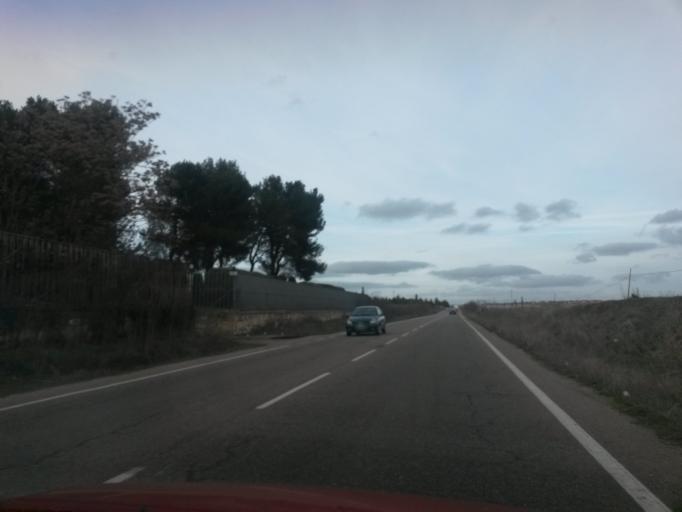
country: ES
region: Castille and Leon
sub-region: Provincia de Salamanca
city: Salamanca
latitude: 40.9867
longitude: -5.6595
